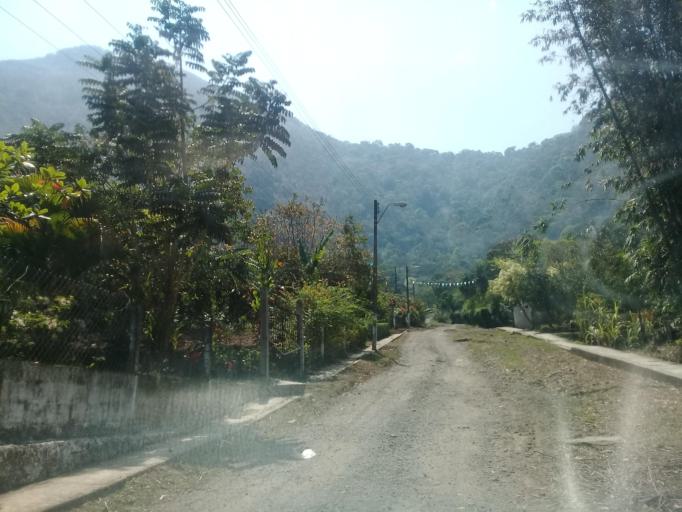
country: MX
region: Veracruz
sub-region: Ixtaczoquitlan
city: Capoluca
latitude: 18.8044
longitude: -96.9856
